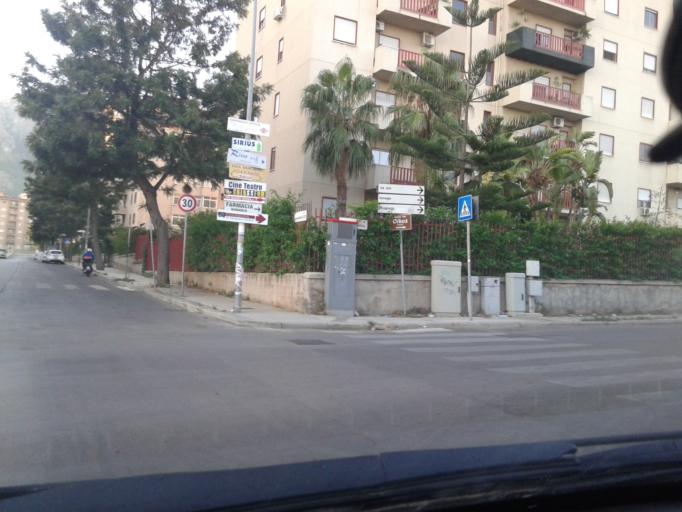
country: IT
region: Sicily
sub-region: Palermo
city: Ciaculli
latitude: 38.0865
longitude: 13.3614
